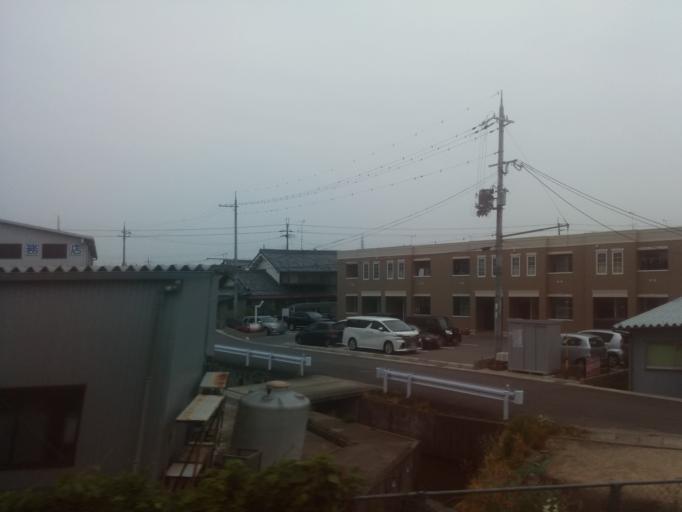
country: JP
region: Shiga Prefecture
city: Moriyama
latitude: 35.0763
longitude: 136.0337
